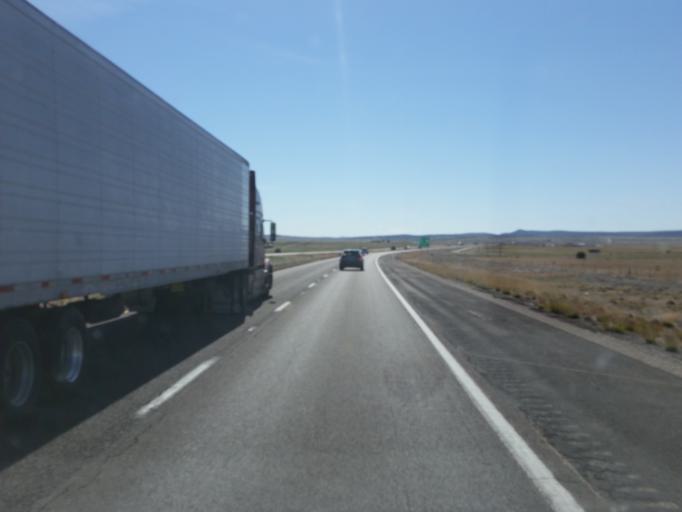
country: US
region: Arizona
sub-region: Yavapai County
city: Paulden
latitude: 35.3158
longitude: -112.8708
